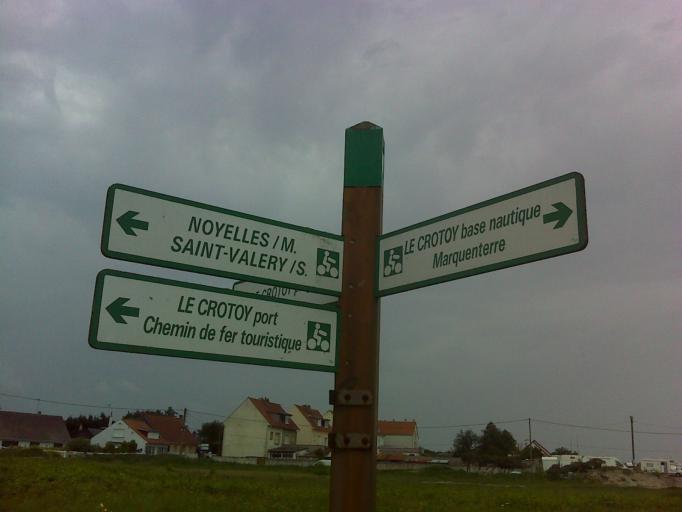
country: FR
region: Picardie
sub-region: Departement de la Somme
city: Le Crotoy
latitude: 50.2288
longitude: 1.6142
